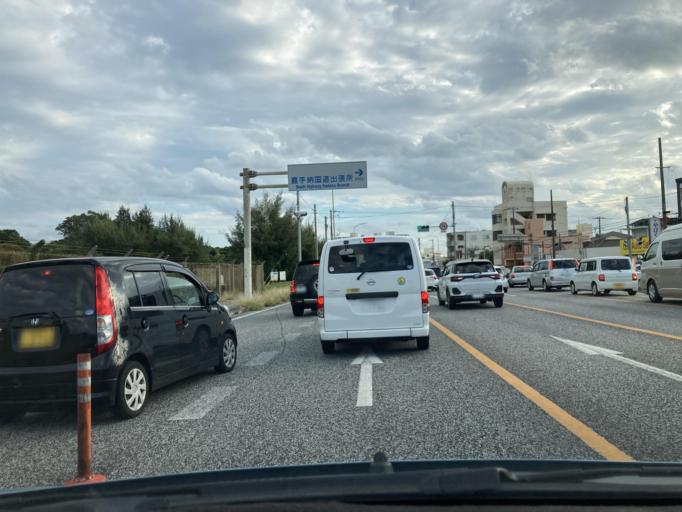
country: JP
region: Okinawa
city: Chatan
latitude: 26.3313
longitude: 127.7518
